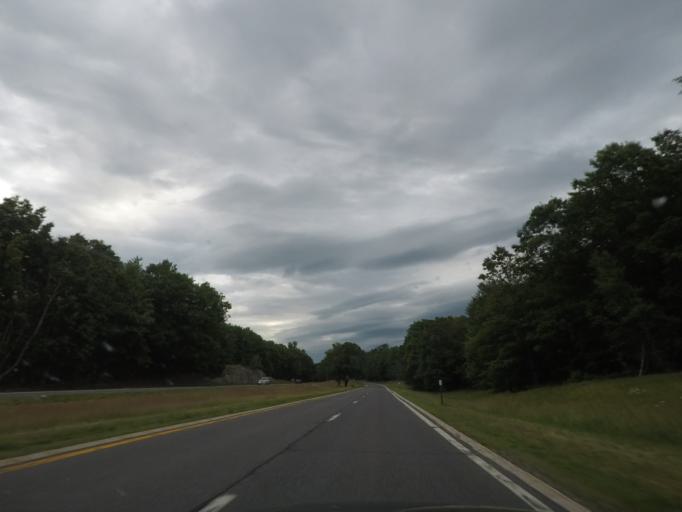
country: US
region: New York
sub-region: Dutchess County
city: Pine Plains
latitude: 42.0371
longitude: -73.7338
